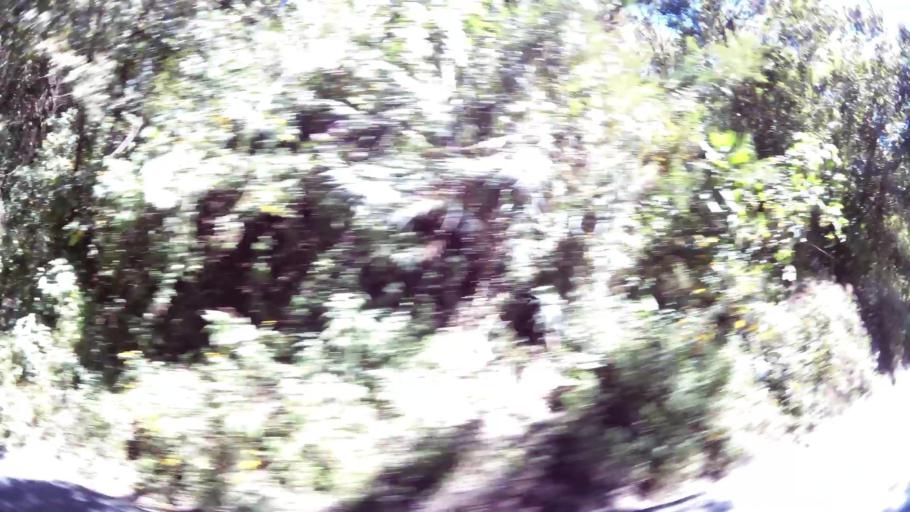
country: GT
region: Solola
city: Solola
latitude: 14.7540
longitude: -91.1723
